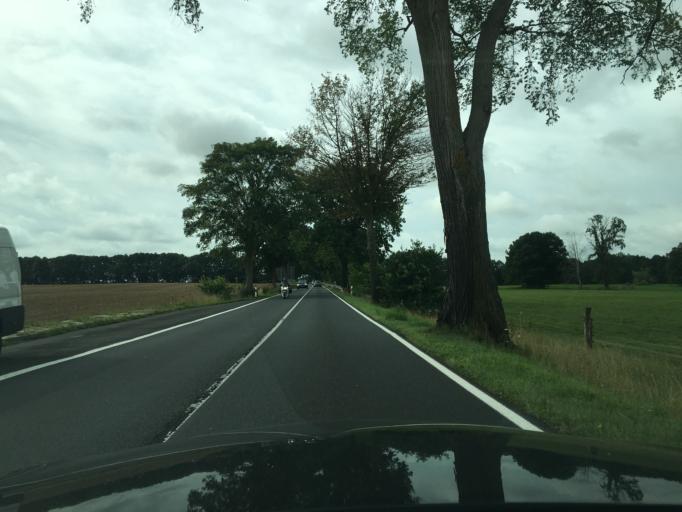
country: DE
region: Brandenburg
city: Gransee
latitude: 52.9649
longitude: 13.1489
